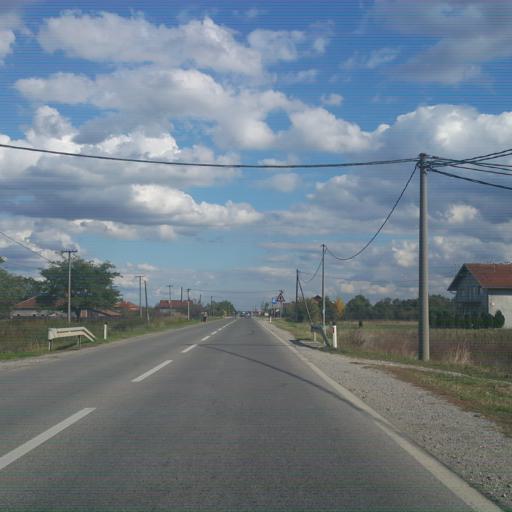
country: RS
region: Central Serbia
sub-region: Rasinski Okrug
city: Trstenik
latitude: 43.5802
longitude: 21.1195
